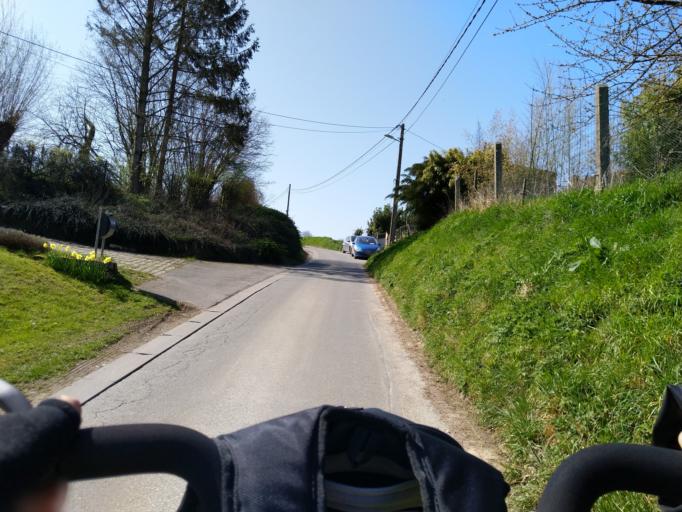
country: BE
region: Wallonia
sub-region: Province du Hainaut
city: Silly
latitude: 50.6421
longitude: 3.9312
